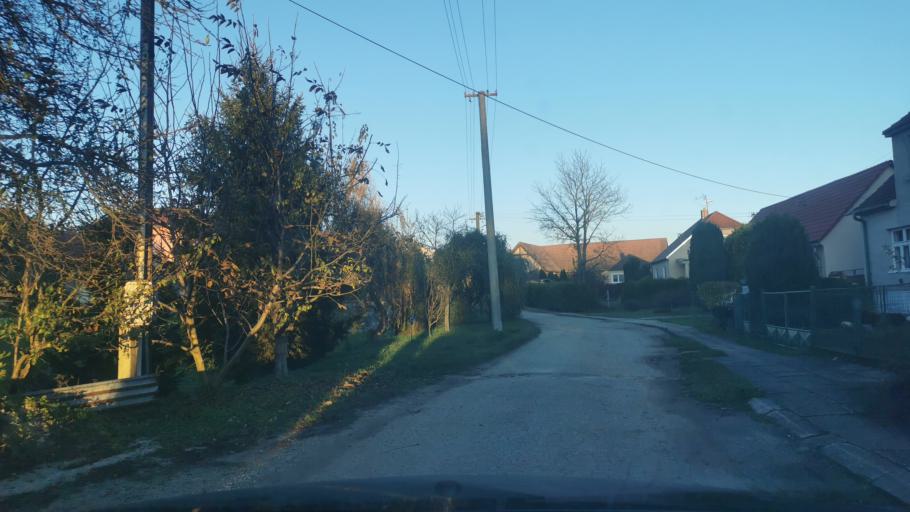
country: SK
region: Trnavsky
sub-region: Okres Senica
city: Senica
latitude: 48.7712
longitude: 17.3136
